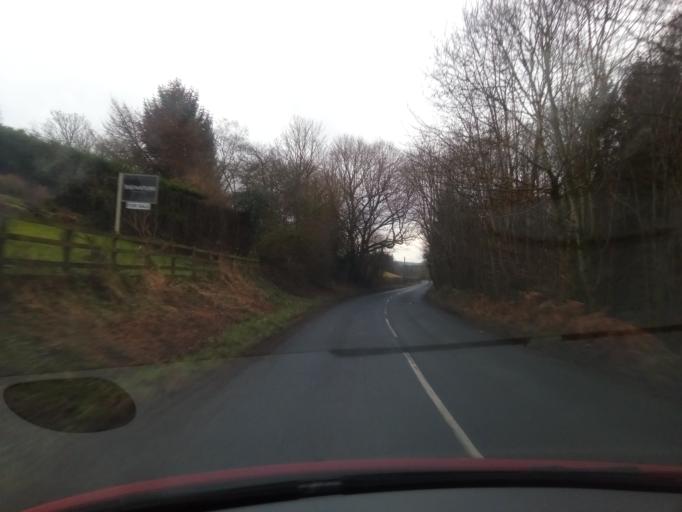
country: GB
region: England
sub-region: Northumberland
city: Whittingham
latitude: 55.4666
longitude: -1.8231
